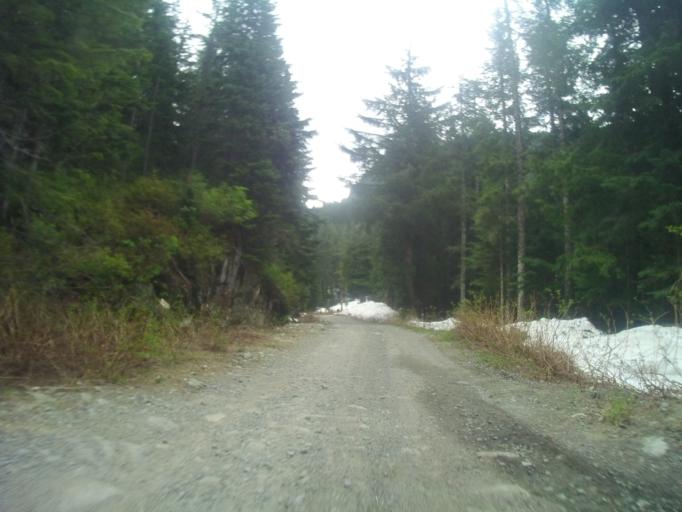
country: CA
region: British Columbia
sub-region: Fraser Valley Regional District
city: North Vancouver
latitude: 49.3859
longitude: -123.0670
